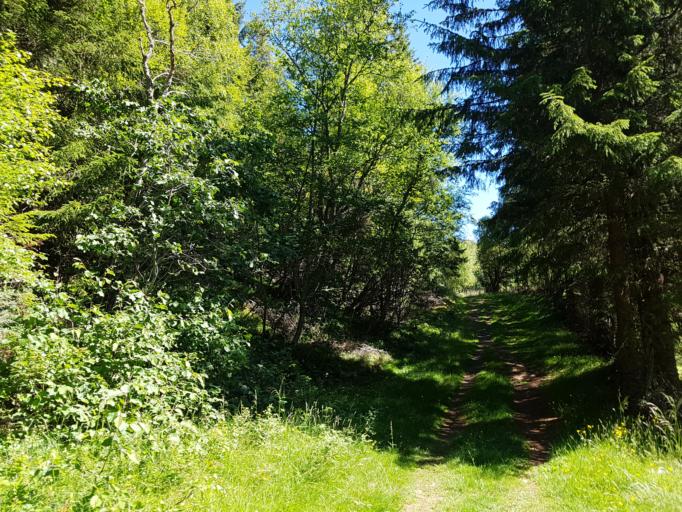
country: NO
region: Sor-Trondelag
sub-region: Skaun
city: Borsa
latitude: 63.4311
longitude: 10.1948
